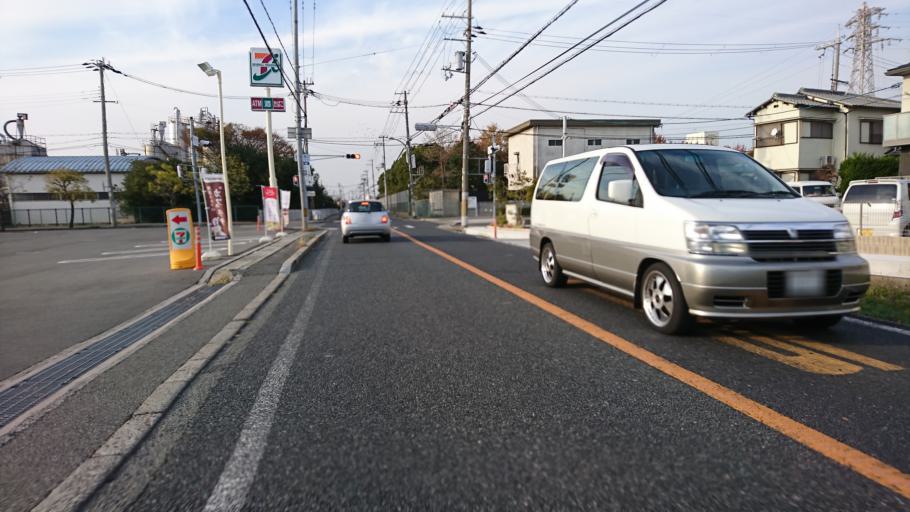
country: JP
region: Hyogo
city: Kakogawacho-honmachi
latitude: 34.7065
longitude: 134.8707
